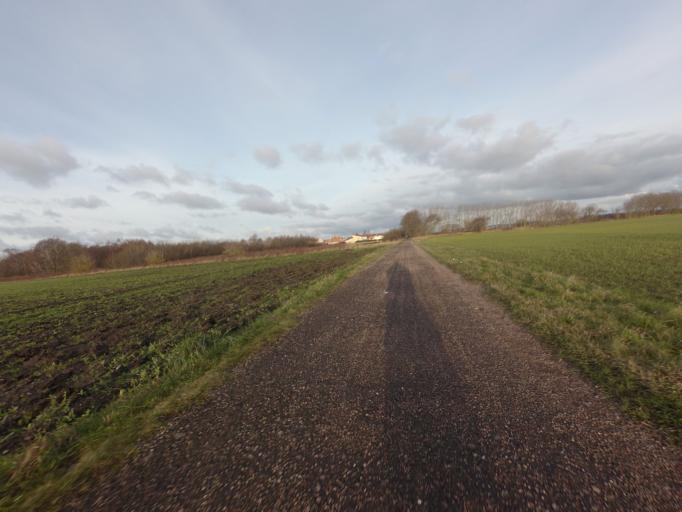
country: SE
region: Skane
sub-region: Hoganas Kommun
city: Hoganas
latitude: 56.1771
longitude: 12.5790
